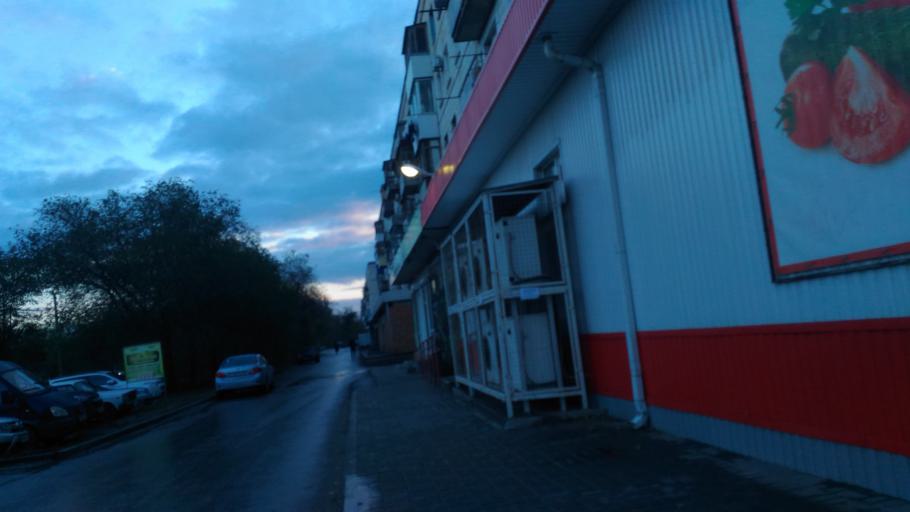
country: RU
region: Volgograd
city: Volgograd
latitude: 48.6540
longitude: 44.4354
